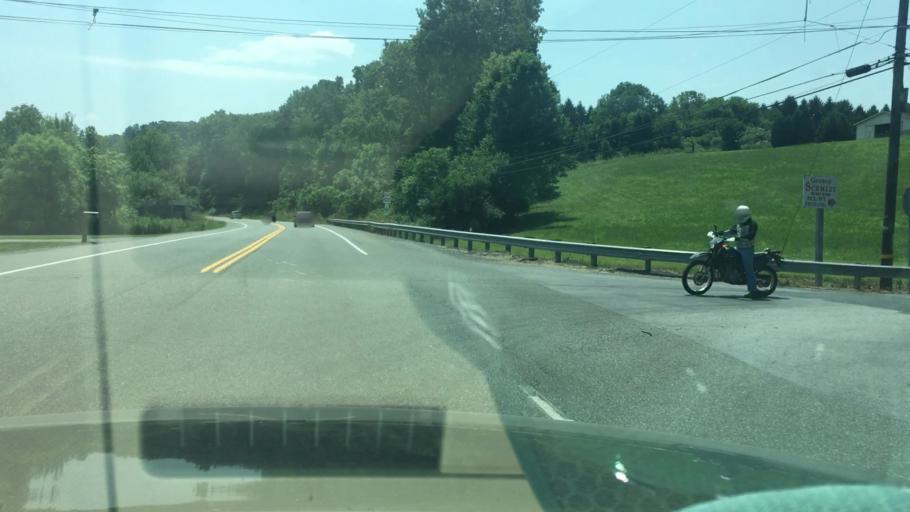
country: US
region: Pennsylvania
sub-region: Lehigh County
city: Schnecksville
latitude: 40.6761
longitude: -75.6928
